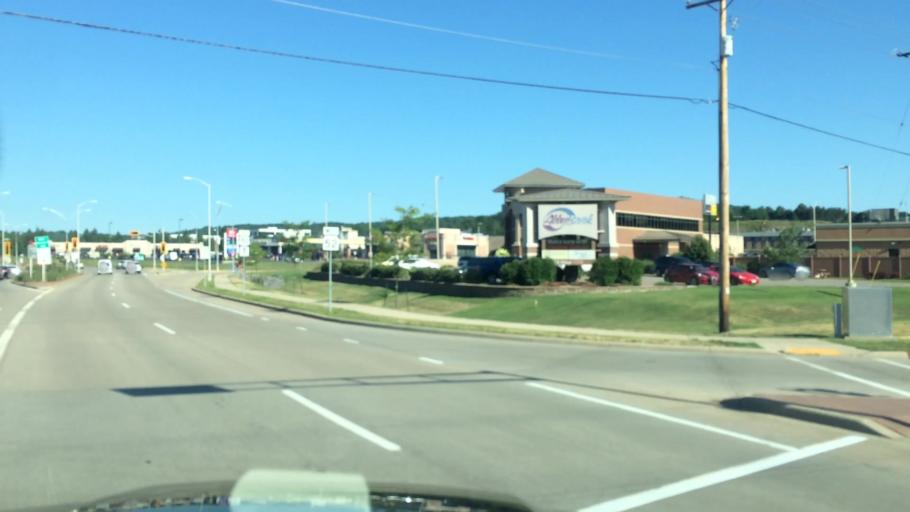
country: US
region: Wisconsin
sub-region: Marathon County
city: Wausau
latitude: 44.9597
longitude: -89.6556
